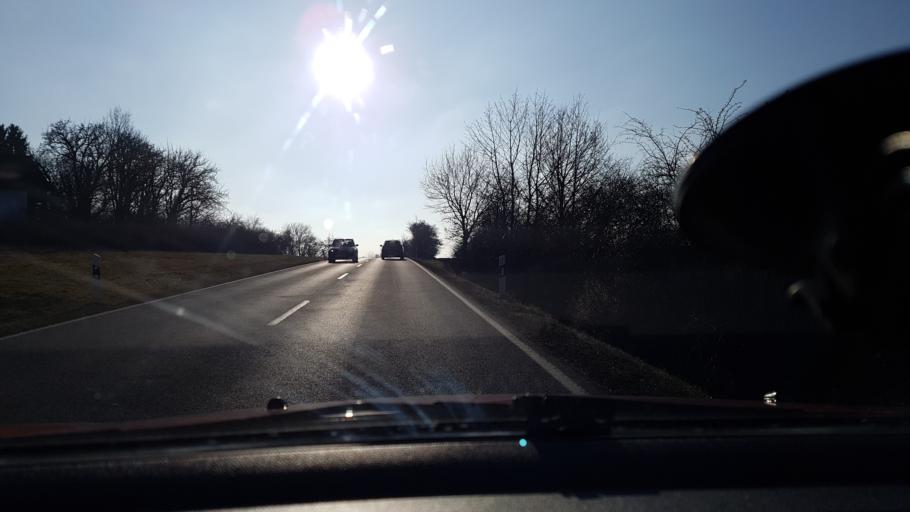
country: DE
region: Bavaria
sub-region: Lower Bavaria
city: Reut
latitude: 48.3359
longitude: 12.9551
